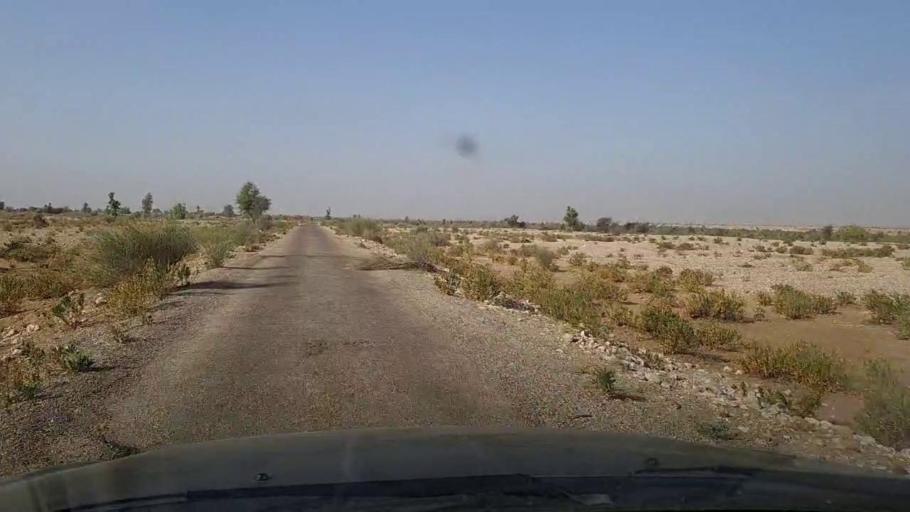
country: PK
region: Sindh
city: Sann
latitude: 25.9531
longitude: 68.0394
